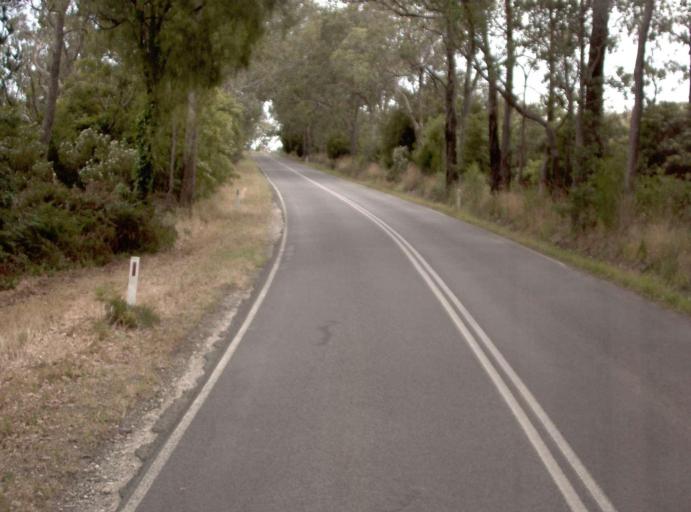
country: AU
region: Victoria
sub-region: Latrobe
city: Traralgon
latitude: -38.1408
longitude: 146.4872
